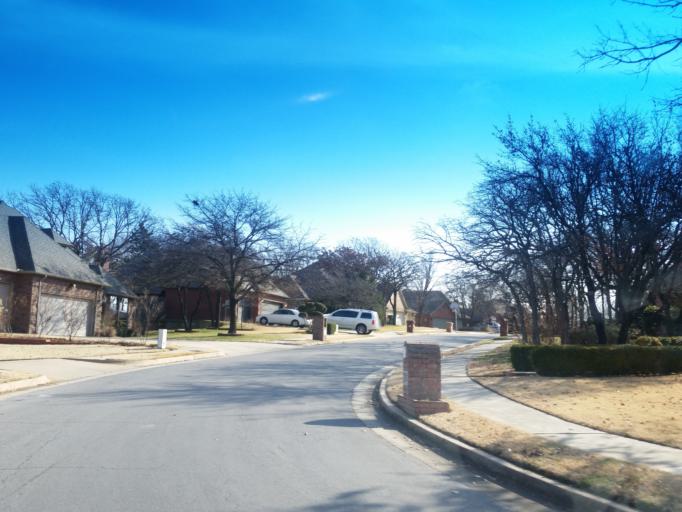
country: US
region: Oklahoma
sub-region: Oklahoma County
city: Edmond
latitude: 35.6455
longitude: -97.4332
